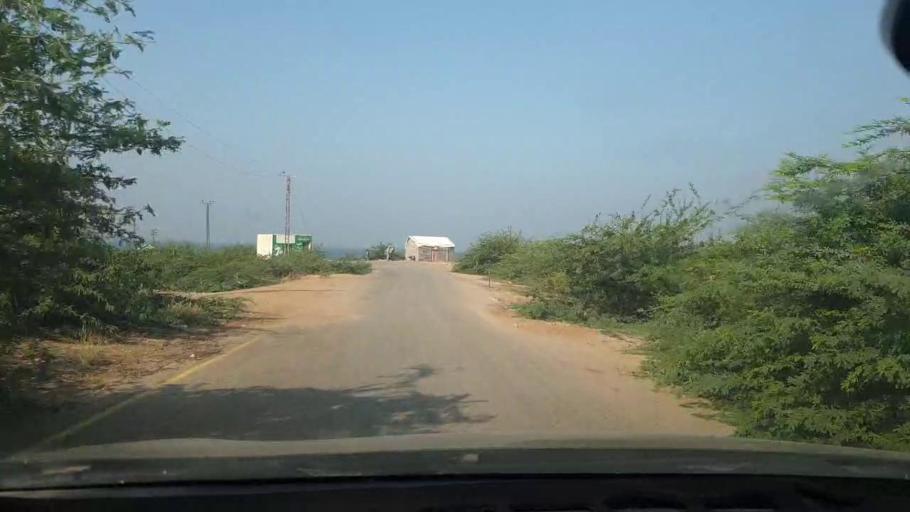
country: PK
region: Balochistan
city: Gadani
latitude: 24.8490
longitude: 66.6640
